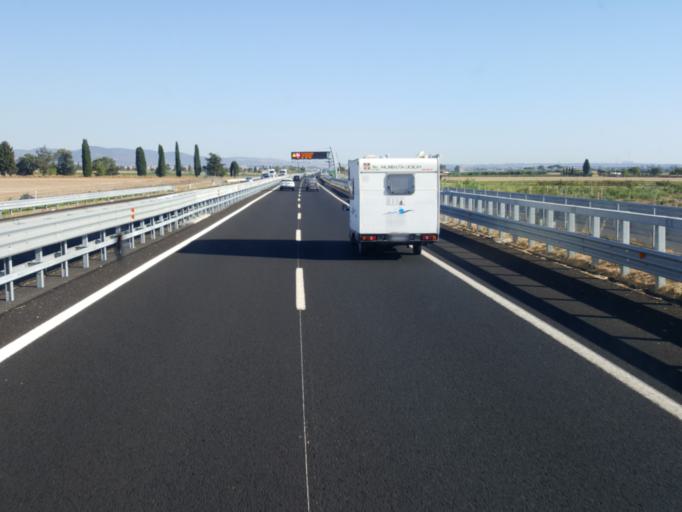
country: IT
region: Latium
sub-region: Provincia di Viterbo
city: Tarquinia
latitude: 42.2313
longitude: 11.7659
